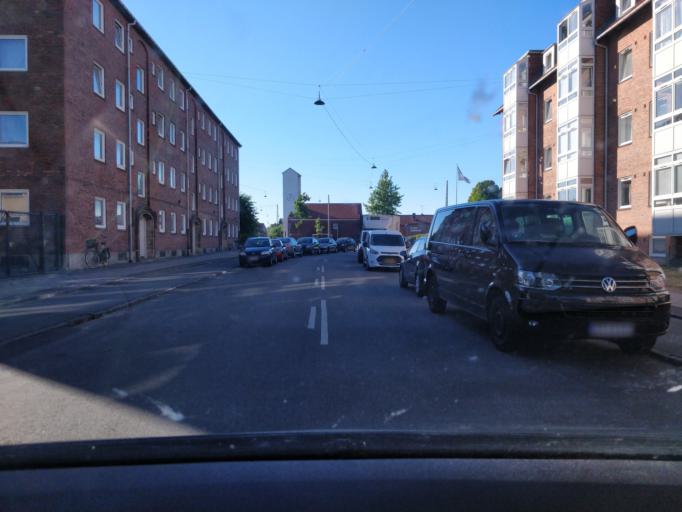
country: DK
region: Capital Region
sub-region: Kobenhavn
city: Vanlose
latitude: 55.6929
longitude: 12.4963
